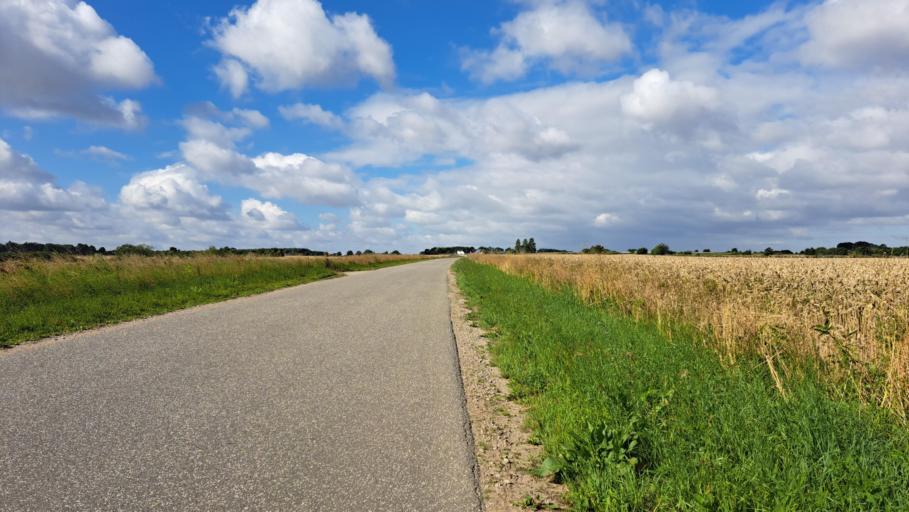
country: DK
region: Central Jutland
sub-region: Hedensted Kommune
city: Hedensted
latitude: 55.7715
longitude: 9.6476
